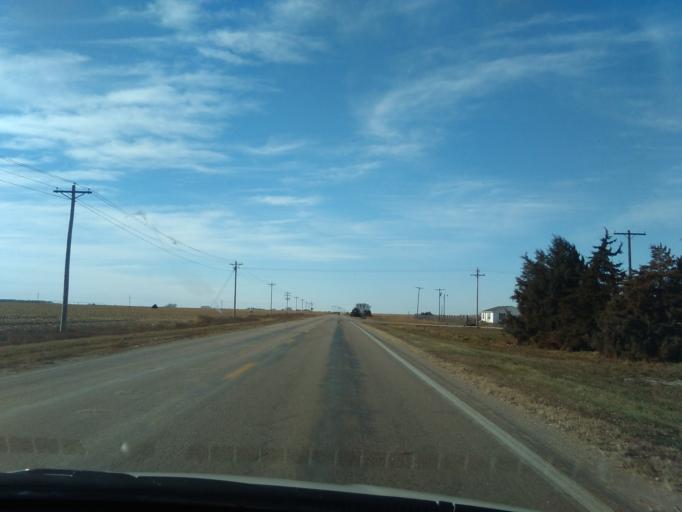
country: US
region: Nebraska
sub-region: Clay County
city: Harvard
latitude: 40.6115
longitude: -98.1013
